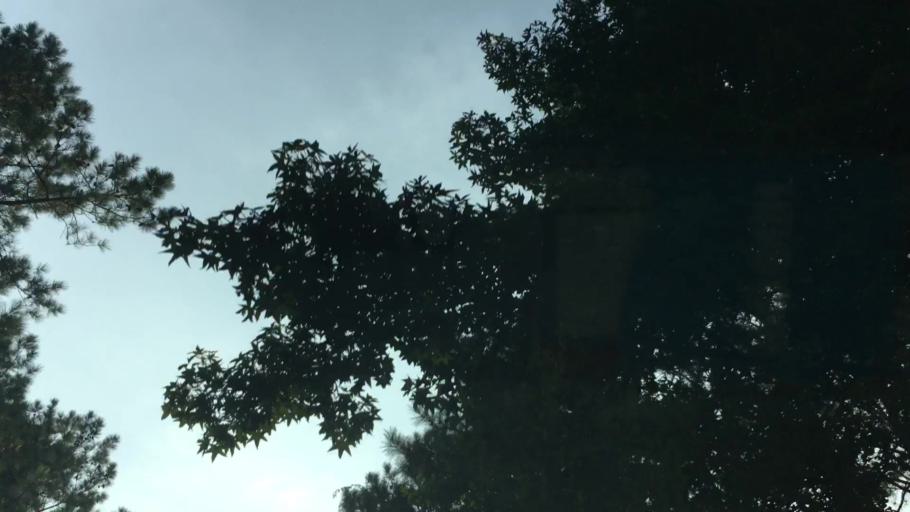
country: US
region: Alabama
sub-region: Bibb County
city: Woodstock
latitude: 33.2136
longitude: -87.0858
